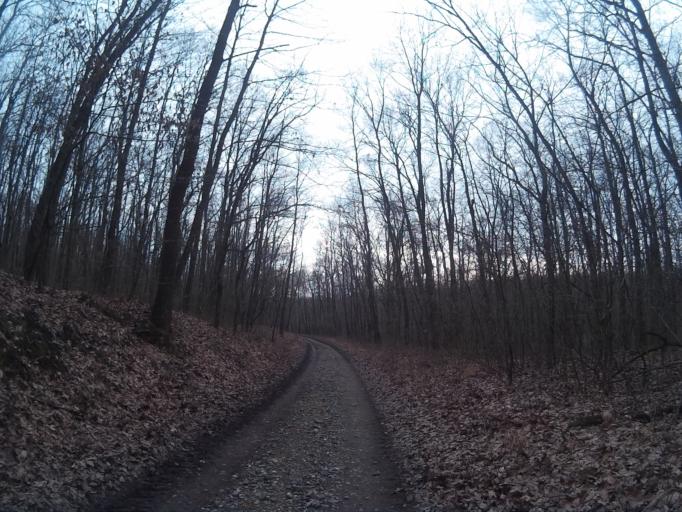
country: HU
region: Komarom-Esztergom
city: Tatabanya
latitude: 47.5886
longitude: 18.4521
